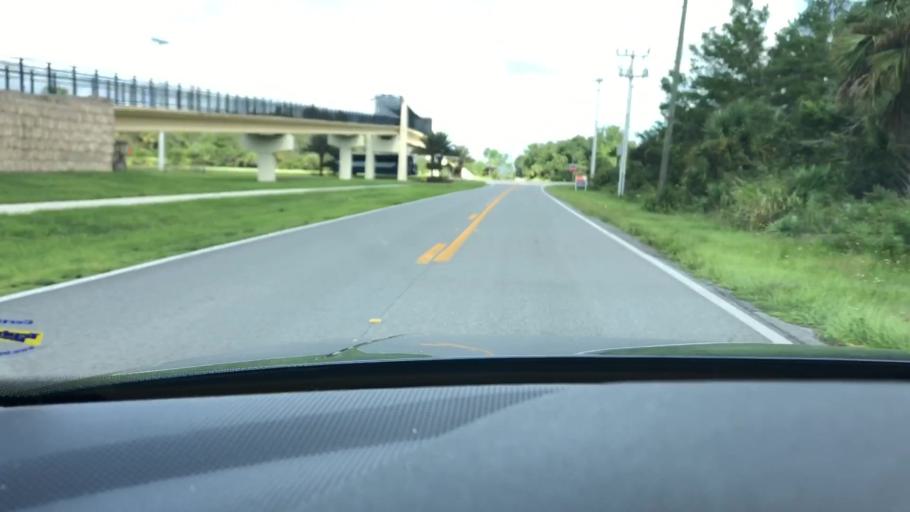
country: US
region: Florida
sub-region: Volusia County
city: Edgewater
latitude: 28.9498
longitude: -80.9449
